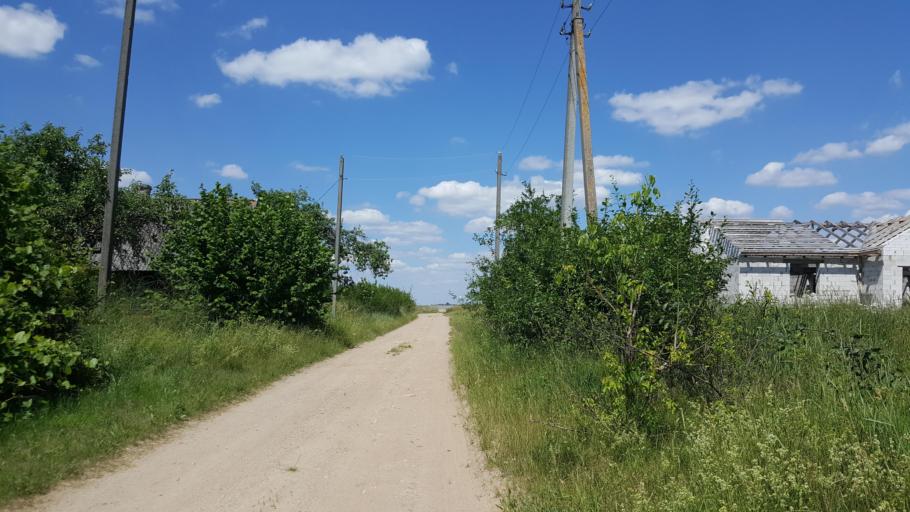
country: BY
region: Brest
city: Kamyanyets
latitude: 52.4060
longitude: 23.7872
